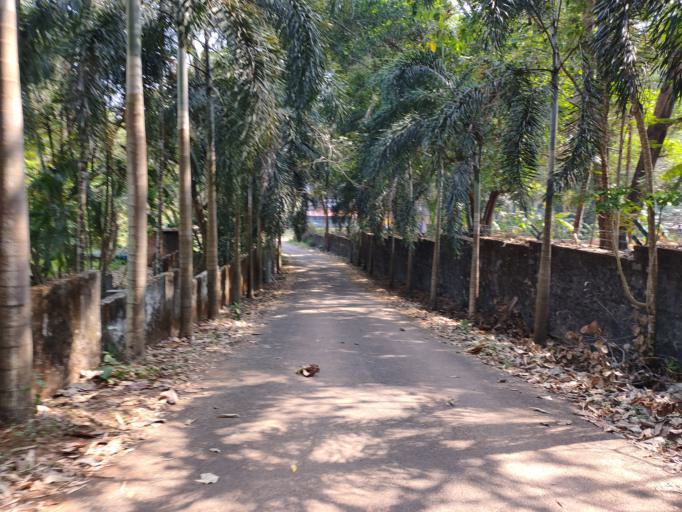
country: IN
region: Kerala
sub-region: Thrissur District
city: Kodungallur
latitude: 10.2340
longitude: 76.2776
